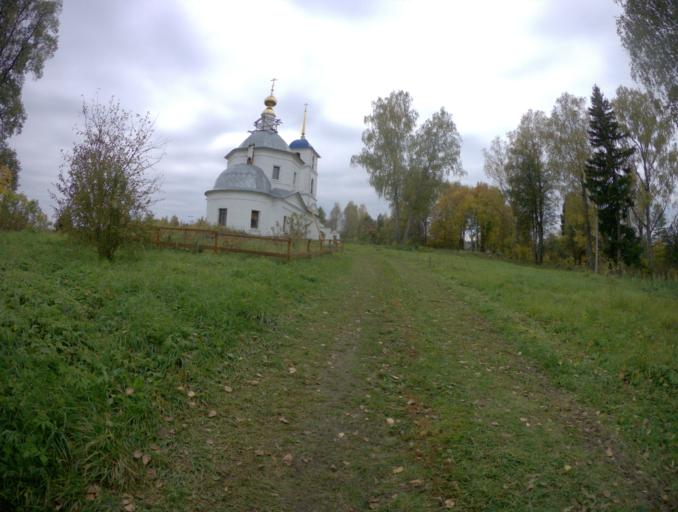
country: RU
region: Vladimir
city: Mstera
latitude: 56.3578
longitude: 41.8659
